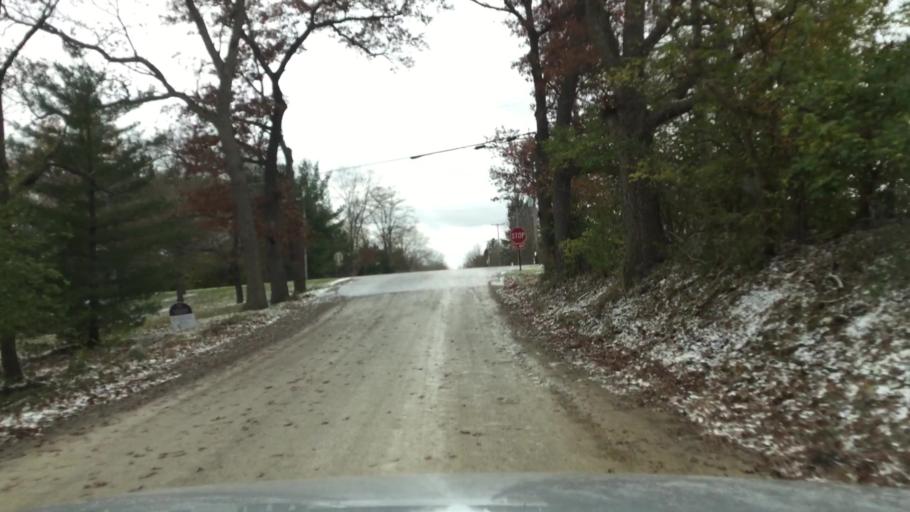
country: US
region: Michigan
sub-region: Livingston County
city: Brighton
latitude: 42.5390
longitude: -83.7156
